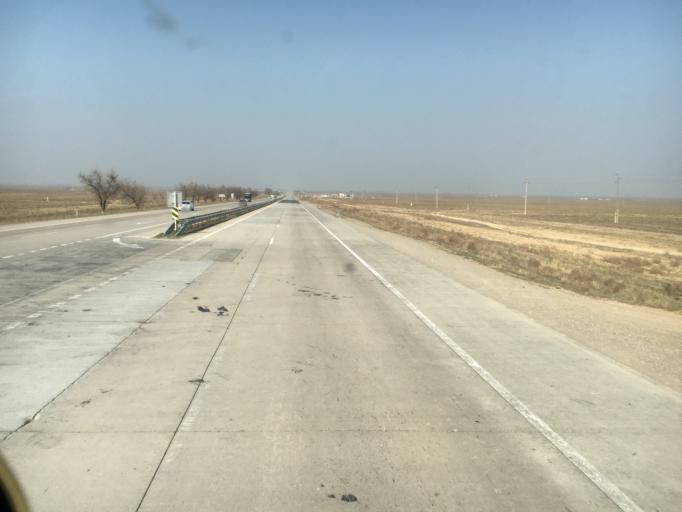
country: KZ
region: Ongtustik Qazaqstan
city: Temirlanovka
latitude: 42.8337
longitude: 69.1214
